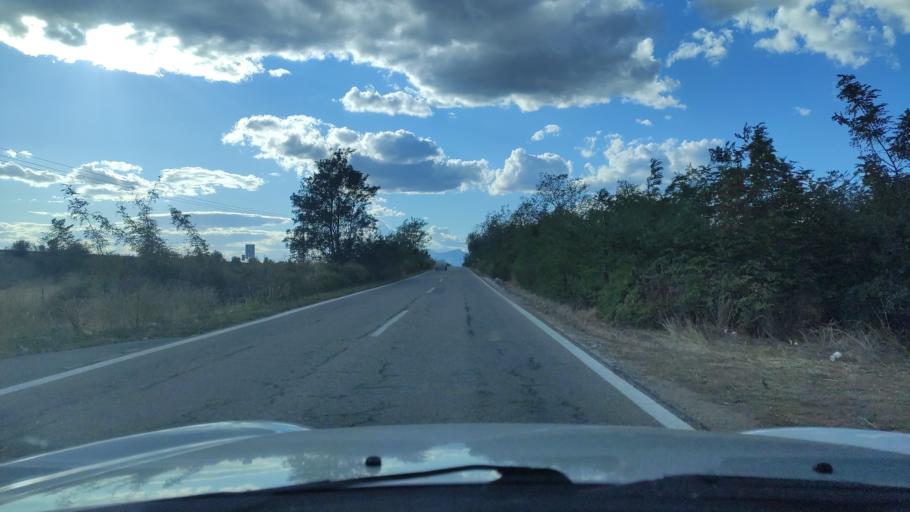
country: GR
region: East Macedonia and Thrace
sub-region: Nomos Xanthis
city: Selero
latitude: 41.1203
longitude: 25.0890
